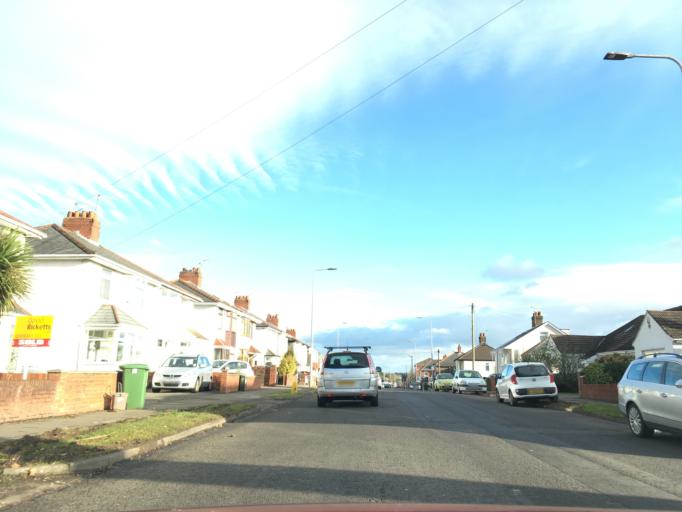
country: GB
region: Wales
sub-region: Cardiff
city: Cardiff
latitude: 51.5192
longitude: -3.2034
